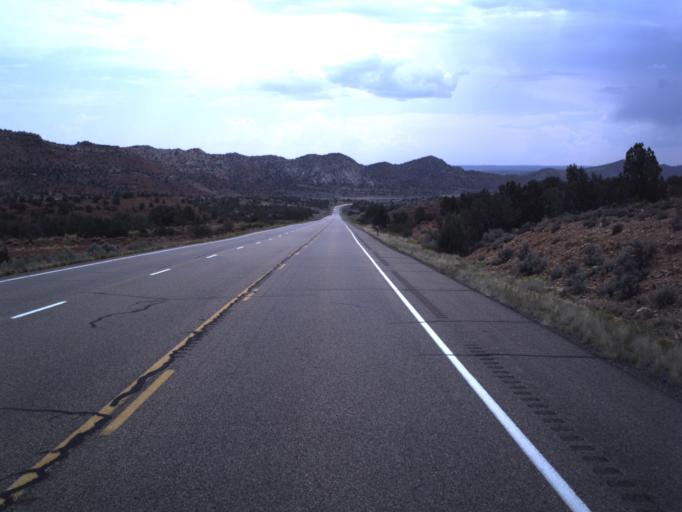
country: US
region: Utah
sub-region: Kane County
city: Kanab
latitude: 37.1775
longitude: -111.9753
